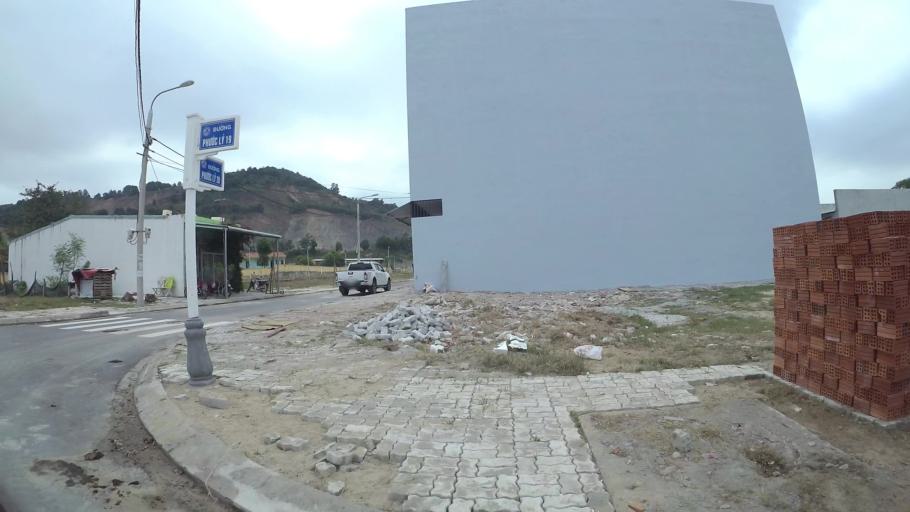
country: VN
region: Da Nang
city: Lien Chieu
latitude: 16.0447
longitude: 108.1647
